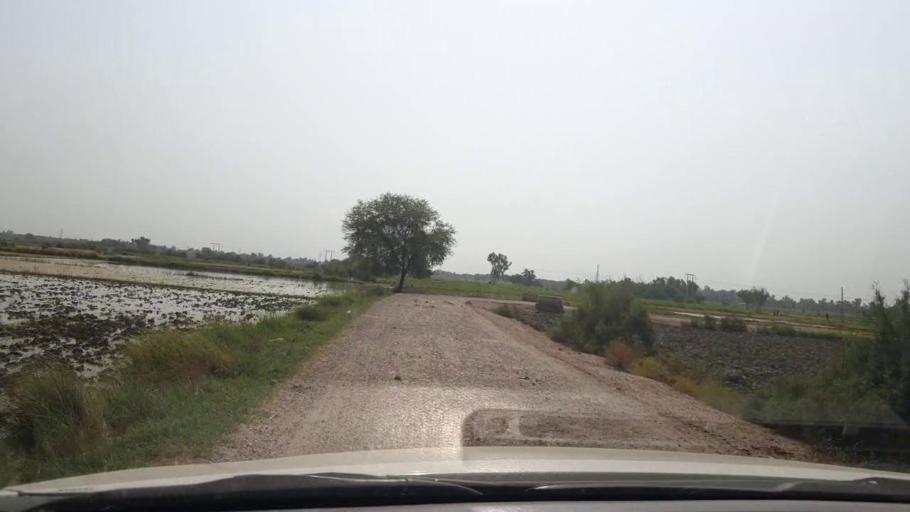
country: PK
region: Sindh
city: Shikarpur
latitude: 27.9818
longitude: 68.6735
